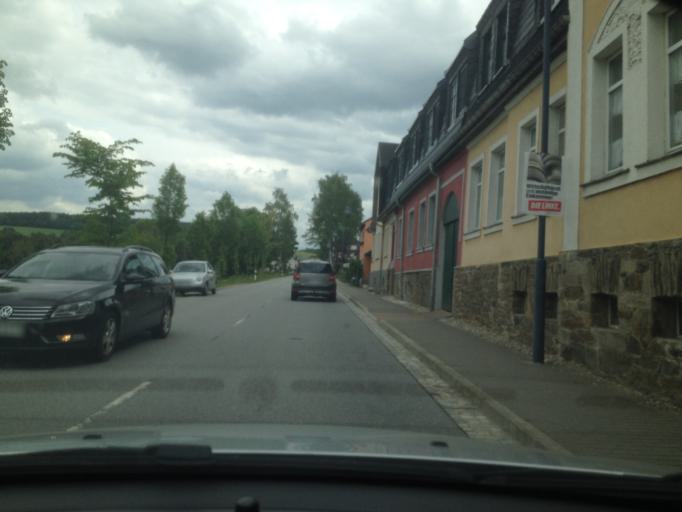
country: DE
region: Saxony
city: Schlettau
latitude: 50.5548
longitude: 12.9555
